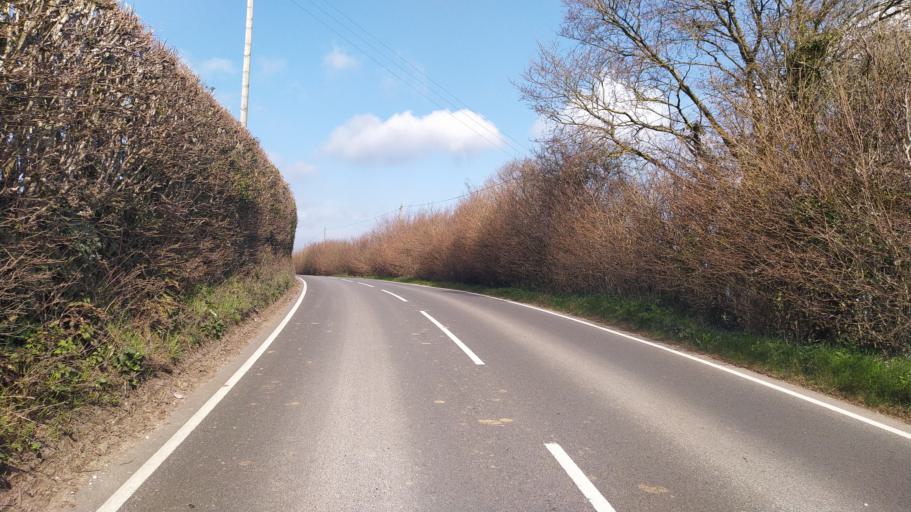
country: GB
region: England
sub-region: Somerset
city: Crewkerne
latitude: 50.8501
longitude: -2.7715
